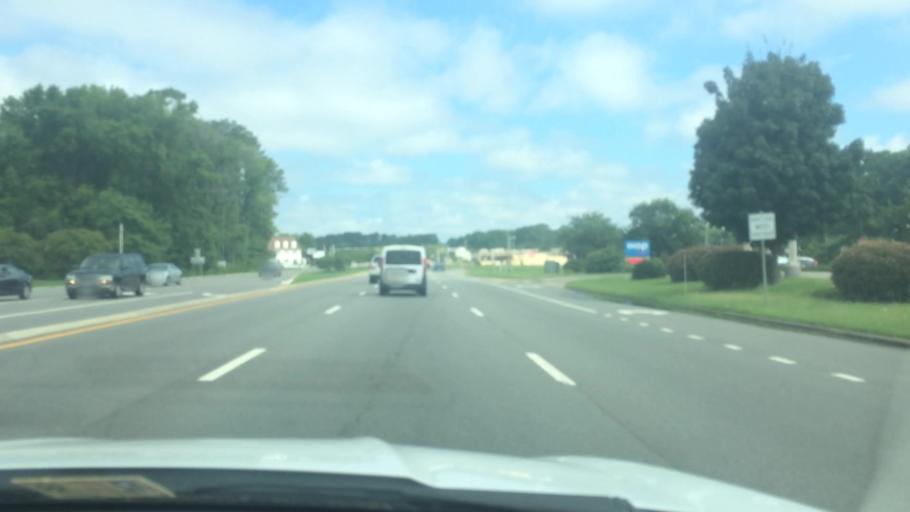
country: US
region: Virginia
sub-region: York County
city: Yorktown
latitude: 37.1609
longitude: -76.4637
